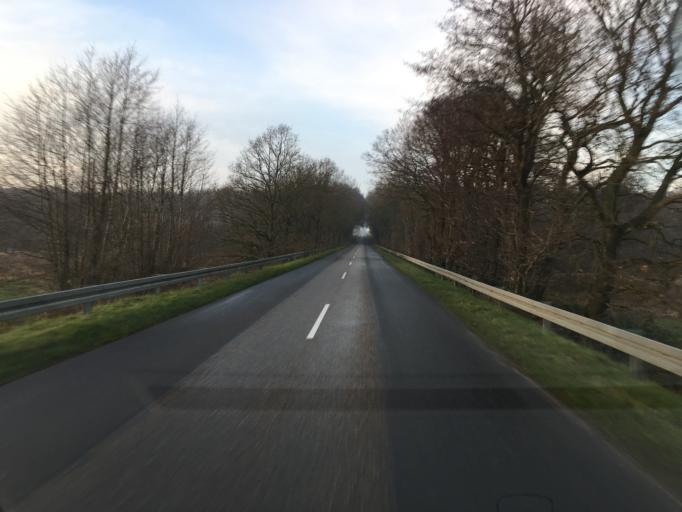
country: DK
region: South Denmark
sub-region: Tonder Kommune
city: Toftlund
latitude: 55.1408
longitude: 9.0543
